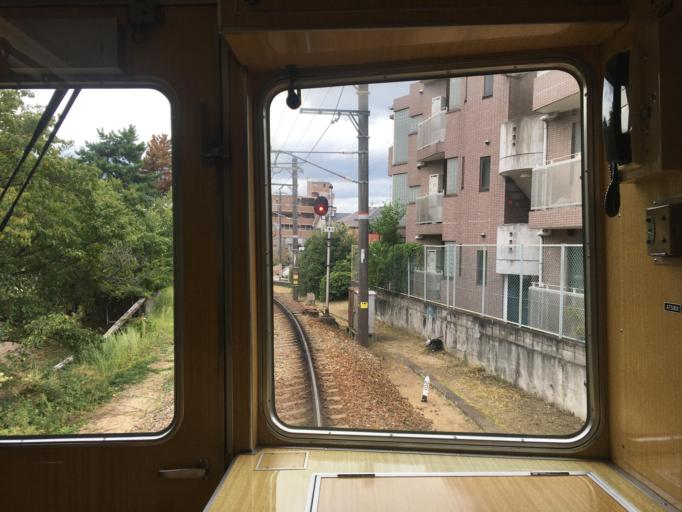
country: JP
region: Hyogo
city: Ashiya
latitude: 34.7527
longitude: 135.3293
